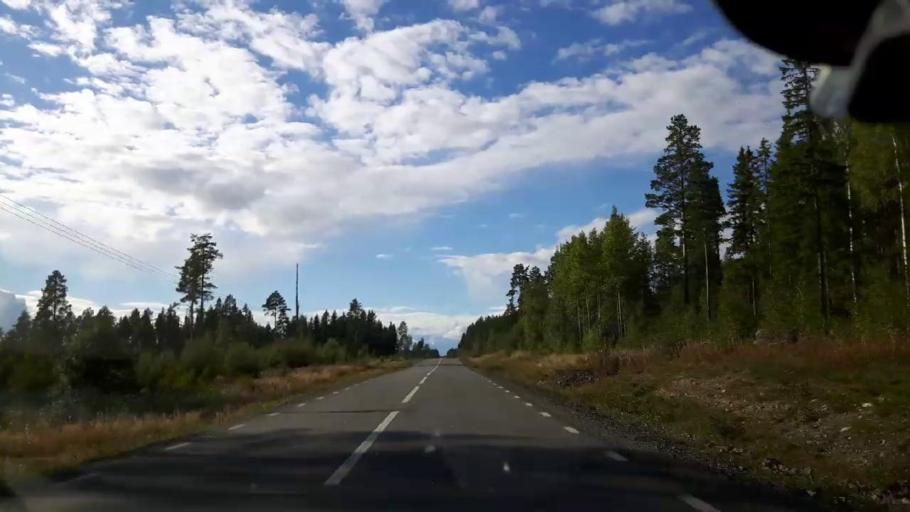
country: SE
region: Jaemtland
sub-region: Stroemsunds Kommun
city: Stroemsund
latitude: 63.5546
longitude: 15.8292
